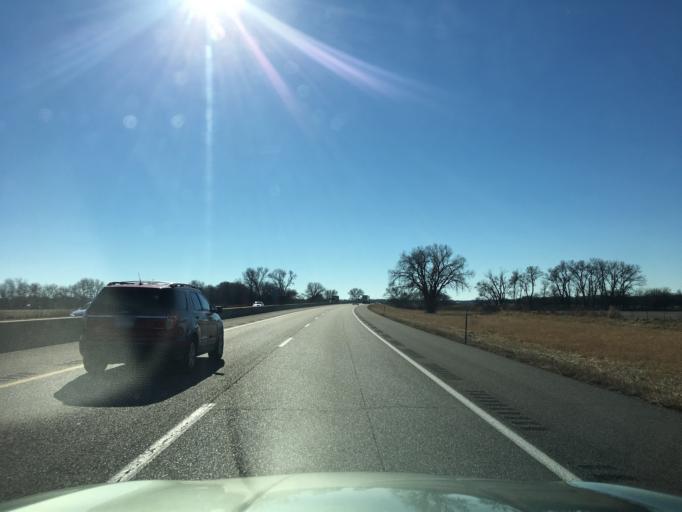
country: US
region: Kansas
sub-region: Sumner County
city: Belle Plaine
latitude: 37.4173
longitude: -97.3212
